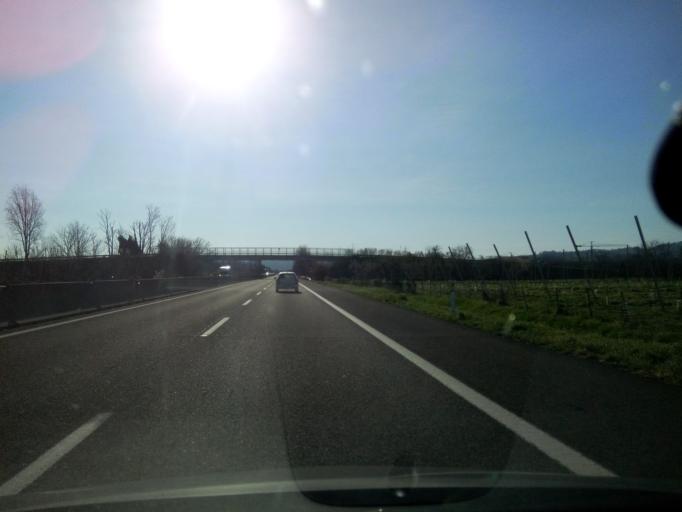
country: IT
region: Emilia-Romagna
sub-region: Provincia di Bologna
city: Zola Predosa
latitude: 44.5010
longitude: 11.2184
